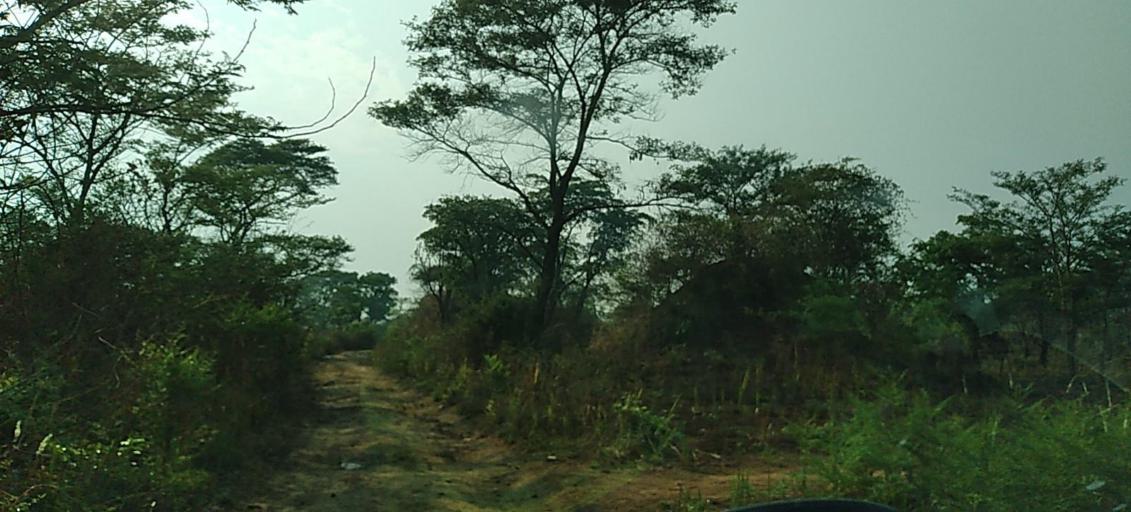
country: ZM
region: North-Western
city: Solwezi
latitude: -12.3948
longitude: 26.5798
